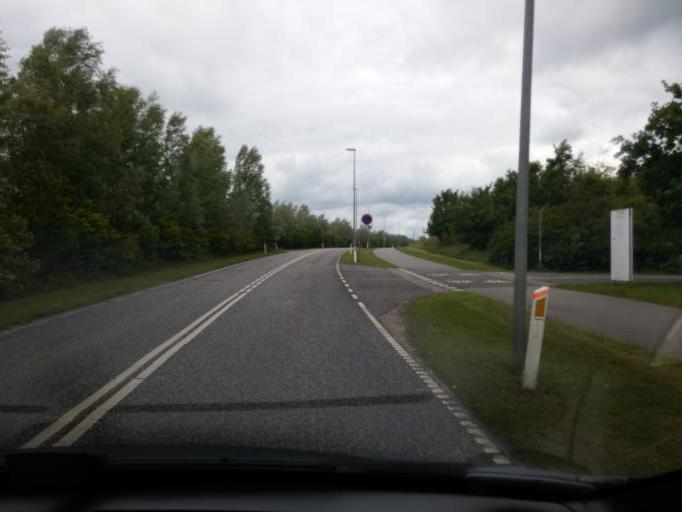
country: DK
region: Capital Region
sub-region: Hillerod Kommune
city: Hillerod
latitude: 55.9207
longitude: 12.2814
